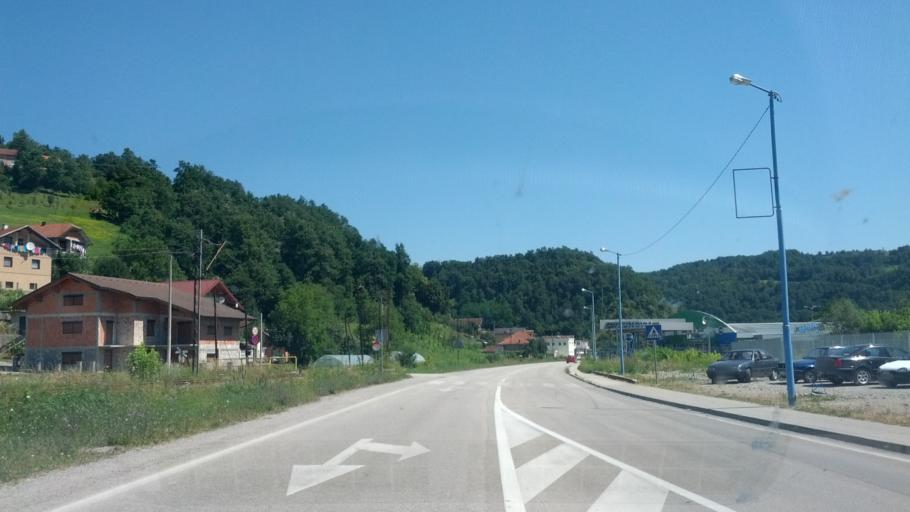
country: BA
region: Federation of Bosnia and Herzegovina
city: Bosanska Krupa
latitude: 44.8959
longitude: 16.1551
